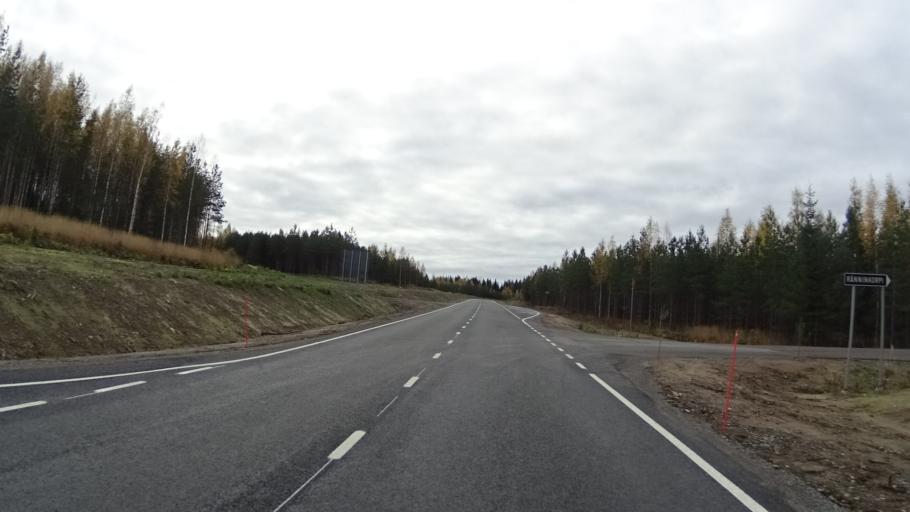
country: FI
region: South Karelia
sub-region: Lappeenranta
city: Taipalsaari
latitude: 61.0298
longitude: 28.0322
